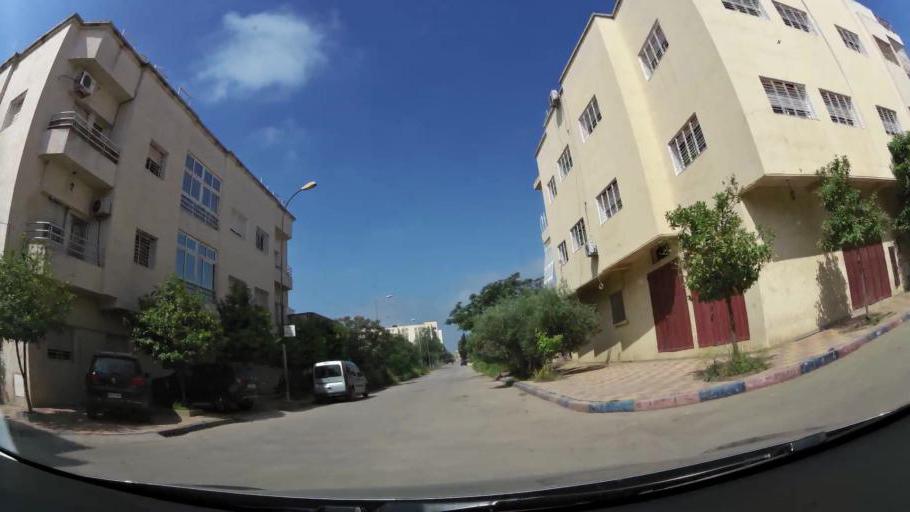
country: MA
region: Fes-Boulemane
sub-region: Fes
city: Fes
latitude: 34.0533
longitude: -5.0296
